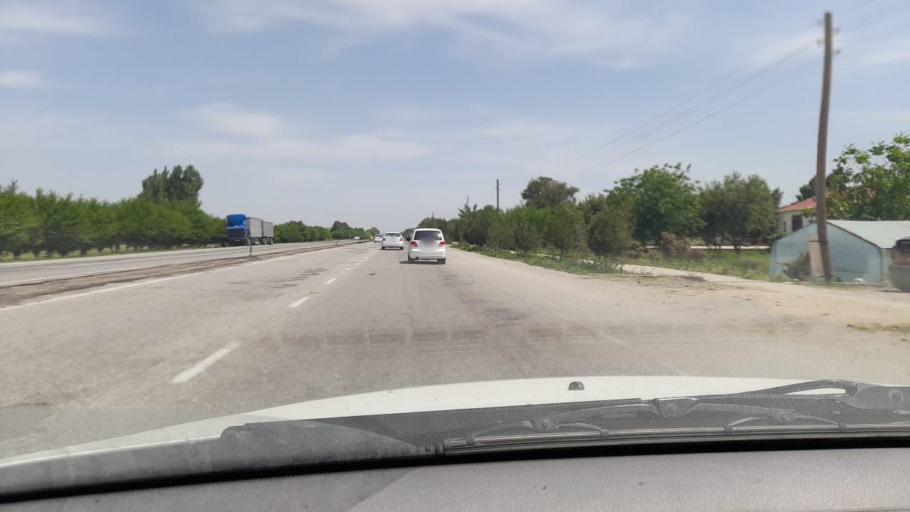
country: UZ
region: Navoiy
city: Beshrabot
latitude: 40.1387
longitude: 65.2816
